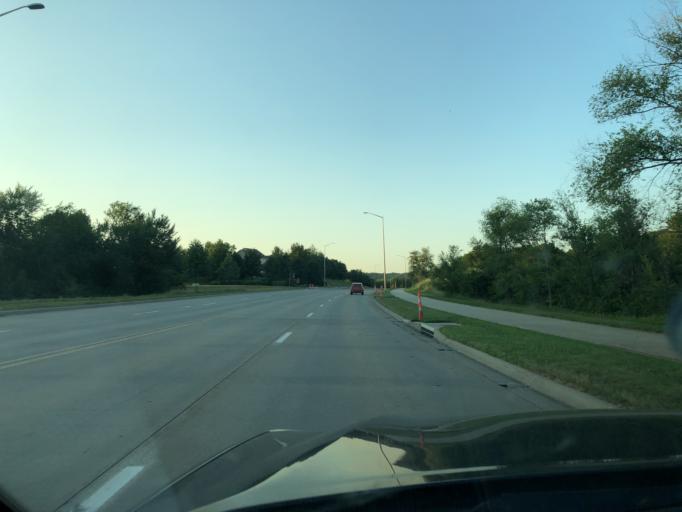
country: US
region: Kansas
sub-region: Leavenworth County
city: Leavenworth
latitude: 39.2762
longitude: -94.9467
